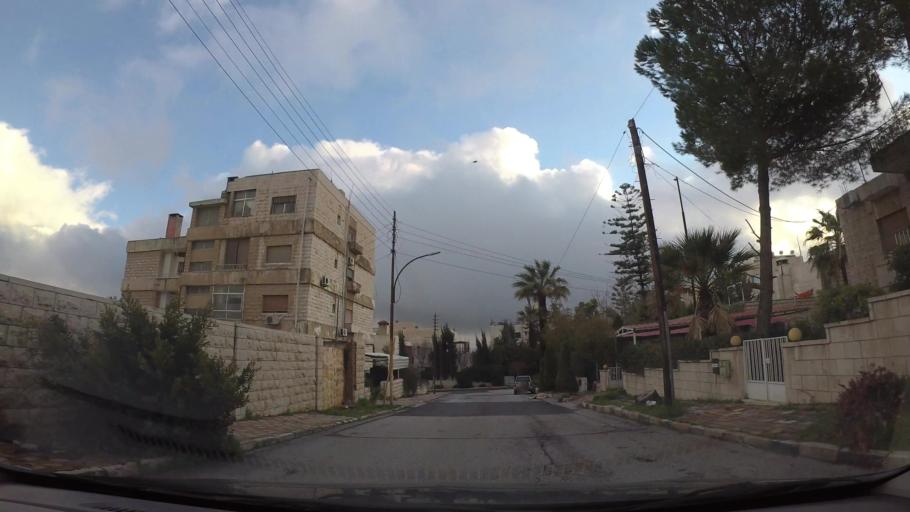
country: JO
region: Amman
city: Amman
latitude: 31.9555
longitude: 35.8916
